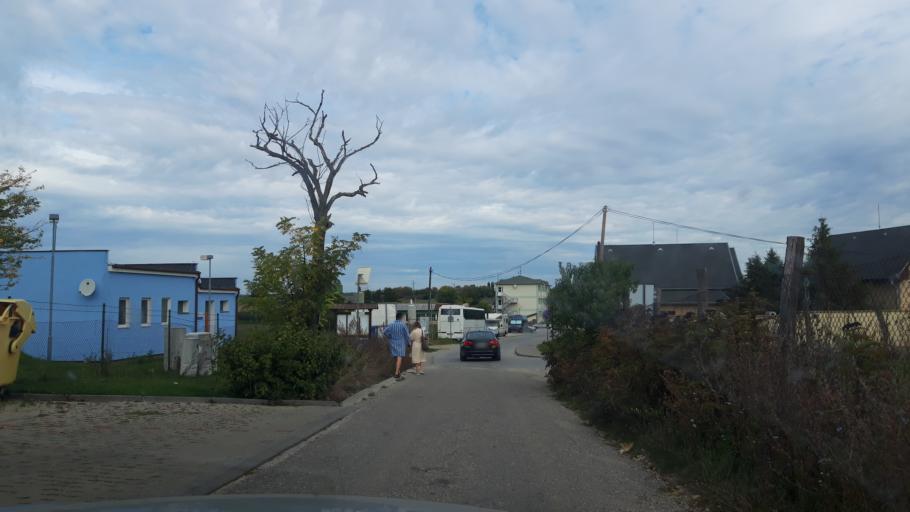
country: SK
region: Nitriansky
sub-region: Okres Nitra
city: Vrable
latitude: 48.0967
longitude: 18.3372
